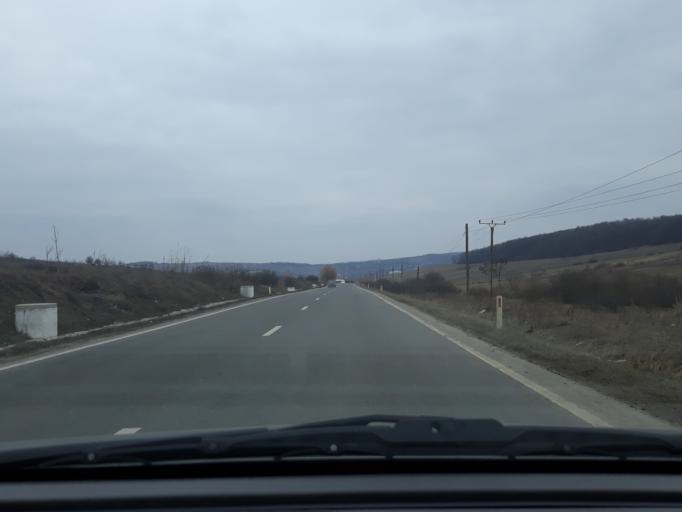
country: RO
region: Salaj
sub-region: Comuna Varsolt
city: Varsolt
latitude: 47.2296
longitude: 22.9716
